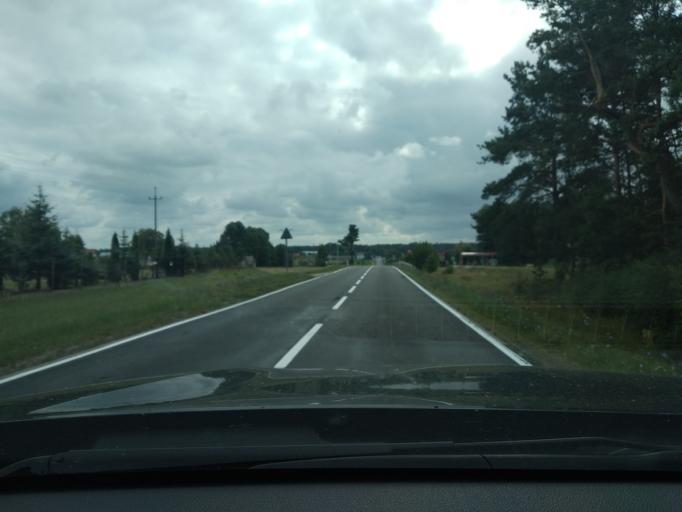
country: PL
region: Masovian Voivodeship
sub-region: Powiat pultuski
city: Obryte
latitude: 52.6511
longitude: 21.2414
